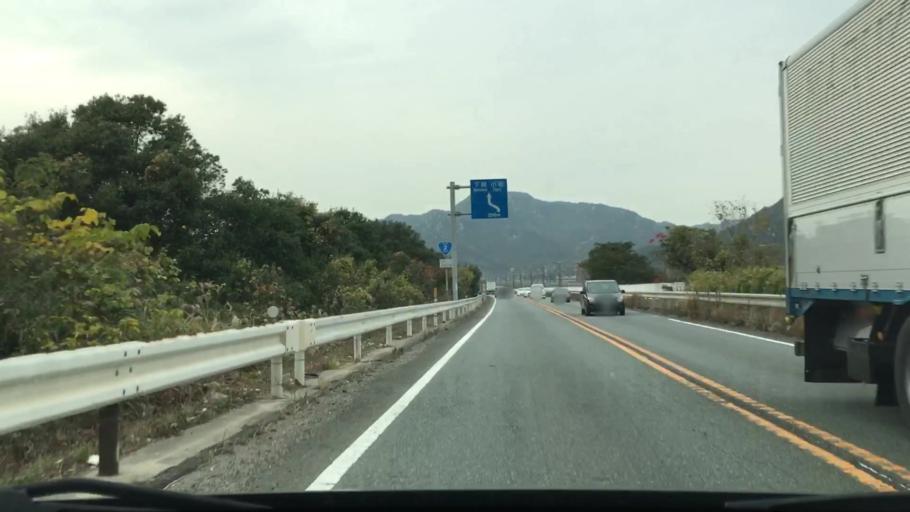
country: JP
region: Yamaguchi
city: Hofu
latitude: 34.0740
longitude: 131.5743
